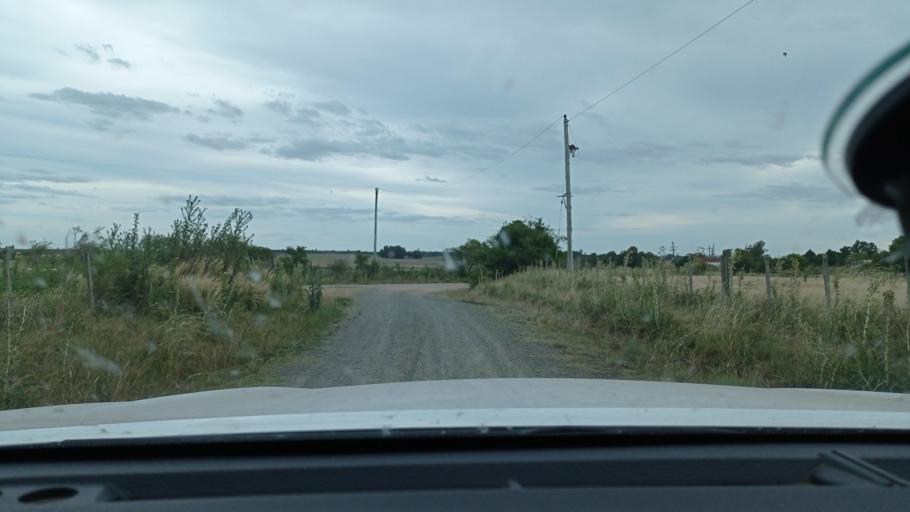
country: UY
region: Florida
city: Casupa
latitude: -34.1503
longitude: -55.7967
